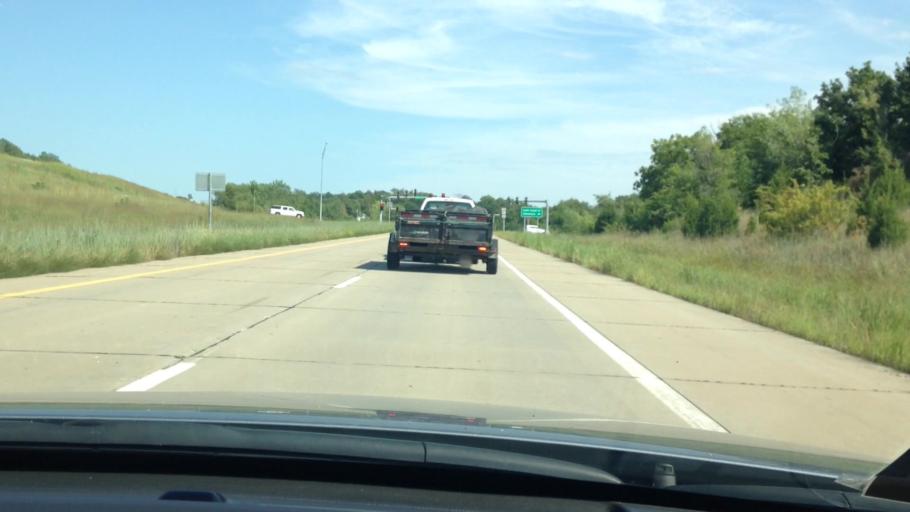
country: US
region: Missouri
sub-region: Jackson County
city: Grandview
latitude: 38.8618
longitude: -94.5874
